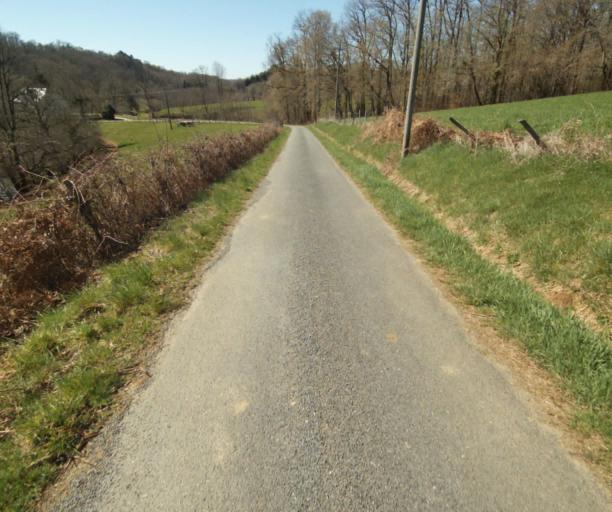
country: FR
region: Limousin
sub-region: Departement de la Correze
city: Chamboulive
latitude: 45.4282
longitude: 1.6795
